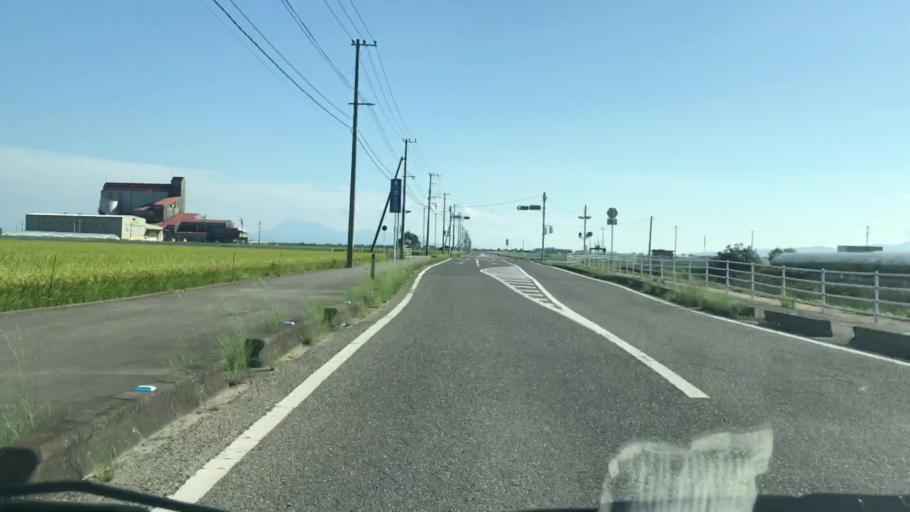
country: JP
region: Saga Prefecture
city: Okawa
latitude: 33.1759
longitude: 130.3119
